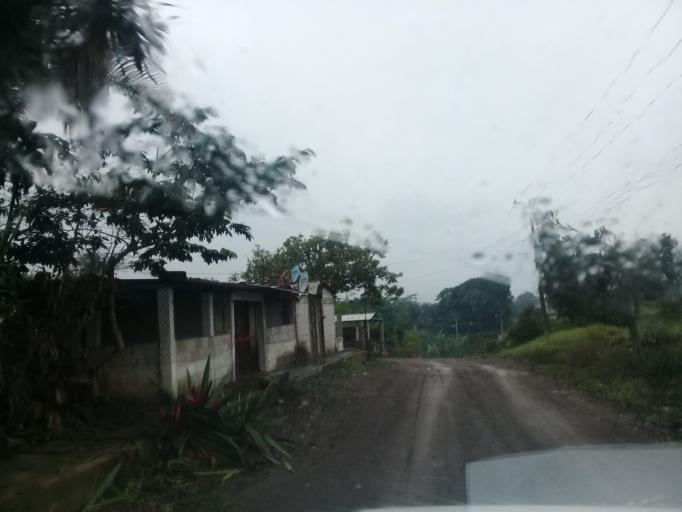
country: MX
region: Veracruz
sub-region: Cordoba
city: San Jose de Tapia
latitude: 18.8463
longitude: -96.9583
